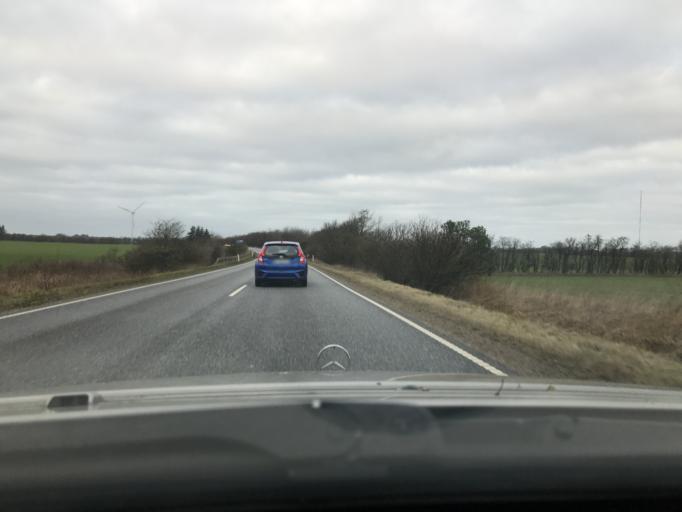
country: DK
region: South Denmark
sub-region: Aabenraa Kommune
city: Rodekro
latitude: 55.1044
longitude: 9.1848
